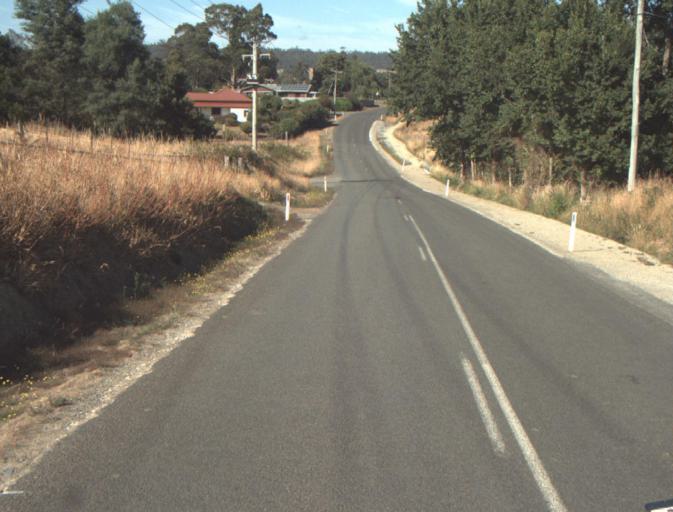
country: AU
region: Tasmania
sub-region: Launceston
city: Mayfield
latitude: -41.1756
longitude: 147.2293
